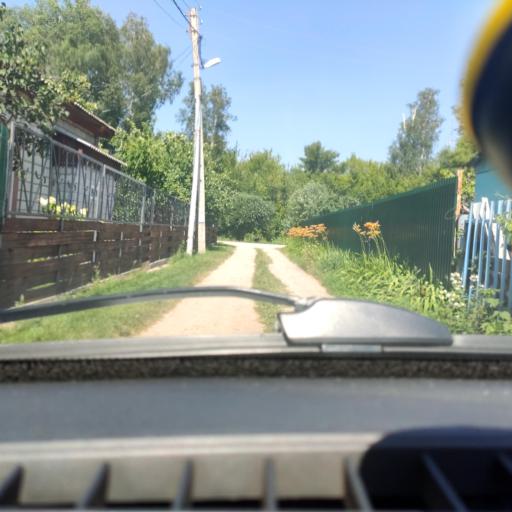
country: RU
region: Samara
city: Tol'yatti
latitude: 53.5985
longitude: 49.3054
